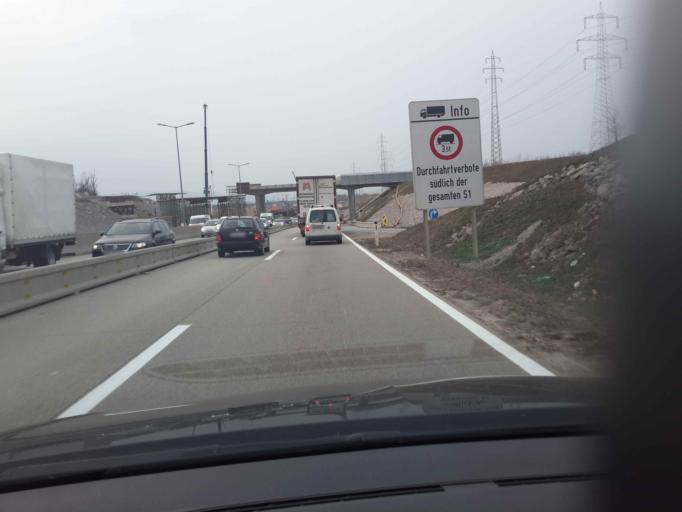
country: AT
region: Lower Austria
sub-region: Politischer Bezirk Modling
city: Hennersdorf
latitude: 48.1272
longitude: 16.3727
